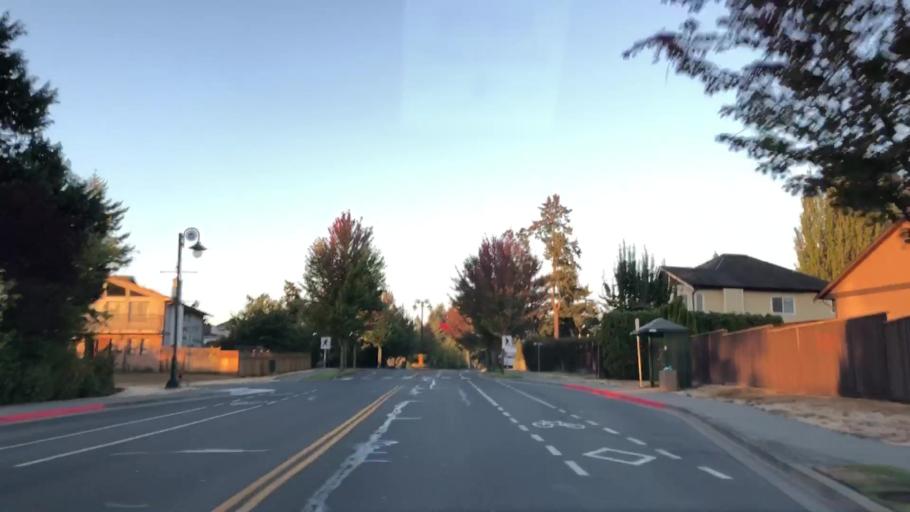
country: CA
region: British Columbia
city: Colwood
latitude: 48.4601
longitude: -123.4330
